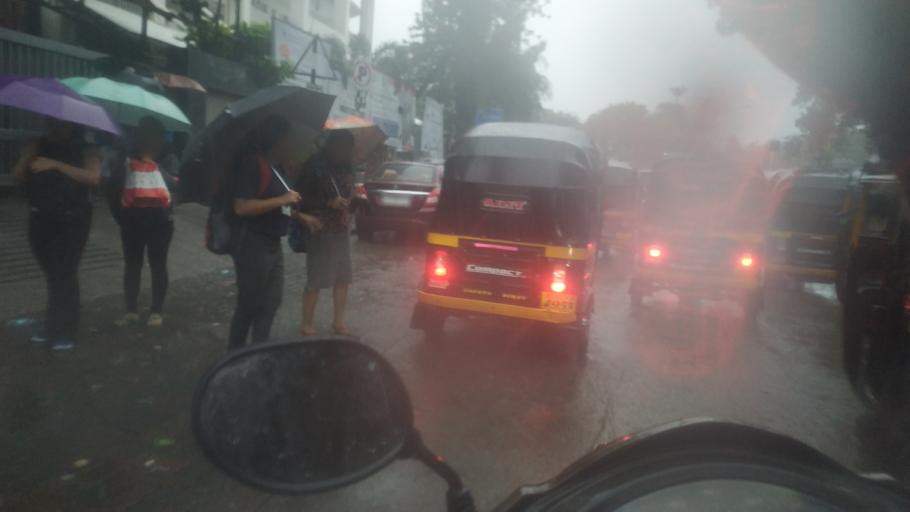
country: IN
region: Maharashtra
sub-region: Mumbai Suburban
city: Mumbai
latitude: 19.1034
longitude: 72.8369
